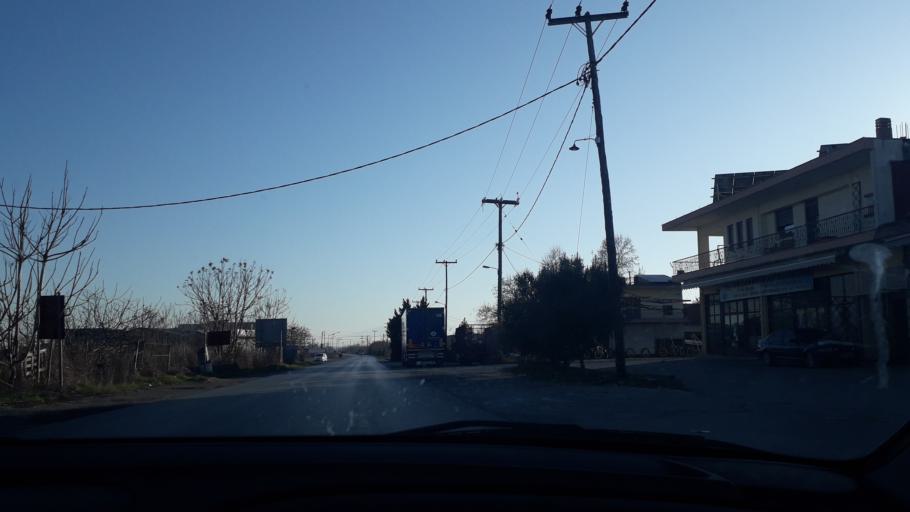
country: GR
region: Central Macedonia
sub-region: Nomos Pellis
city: Giannitsa
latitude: 40.7841
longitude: 22.4047
